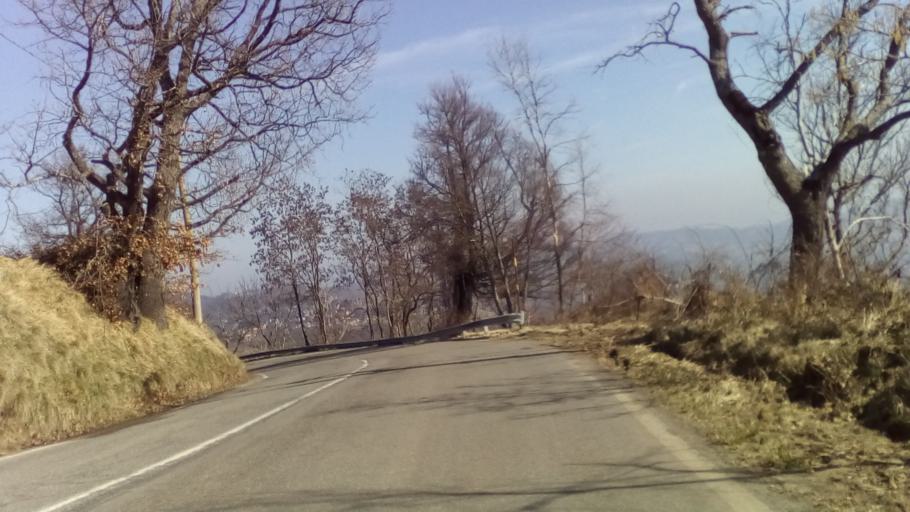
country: IT
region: Emilia-Romagna
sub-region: Provincia di Modena
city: Lama
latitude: 44.2918
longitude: 10.7079
